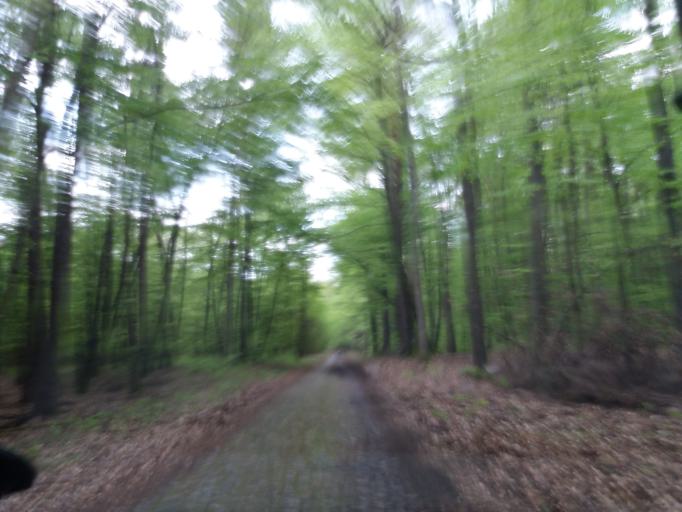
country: PL
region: West Pomeranian Voivodeship
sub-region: Powiat choszczenski
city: Drawno
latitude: 53.1051
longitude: 15.8870
